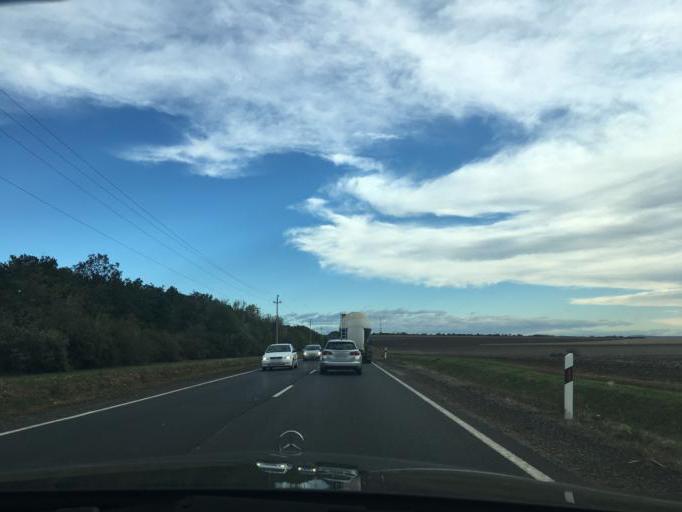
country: HU
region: Borsod-Abauj-Zemplen
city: Arnot
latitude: 48.1382
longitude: 20.8831
